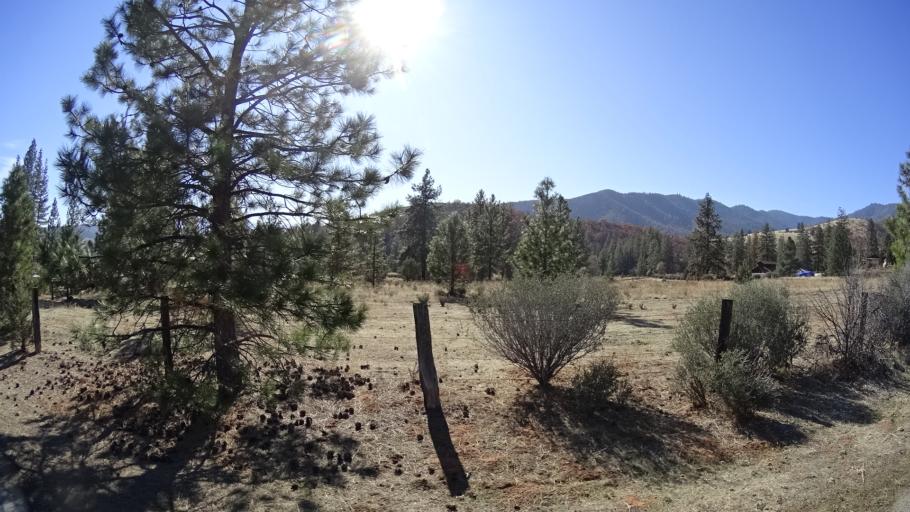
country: US
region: California
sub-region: Siskiyou County
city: Yreka
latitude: 41.7671
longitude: -122.6298
